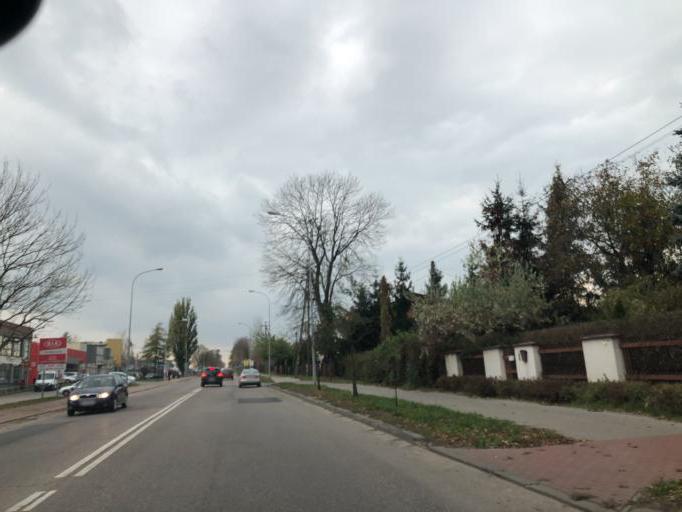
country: PL
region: Podlasie
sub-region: Lomza
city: Lomza
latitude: 53.1757
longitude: 22.0415
